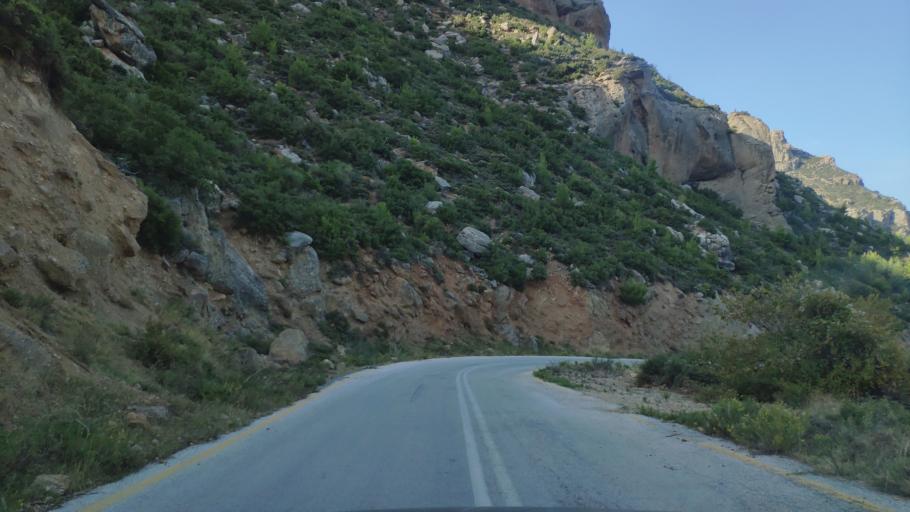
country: GR
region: West Greece
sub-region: Nomos Achaias
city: Aiyira
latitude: 38.0635
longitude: 22.3780
